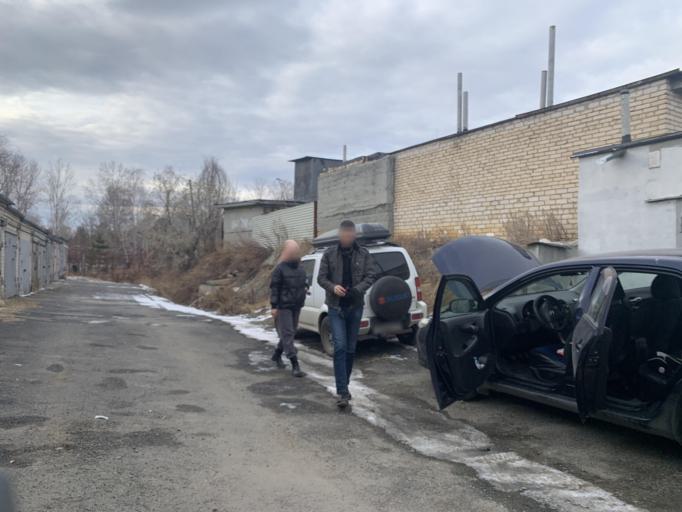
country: RU
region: Chelyabinsk
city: Roshchino
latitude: 55.1883
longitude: 61.2661
